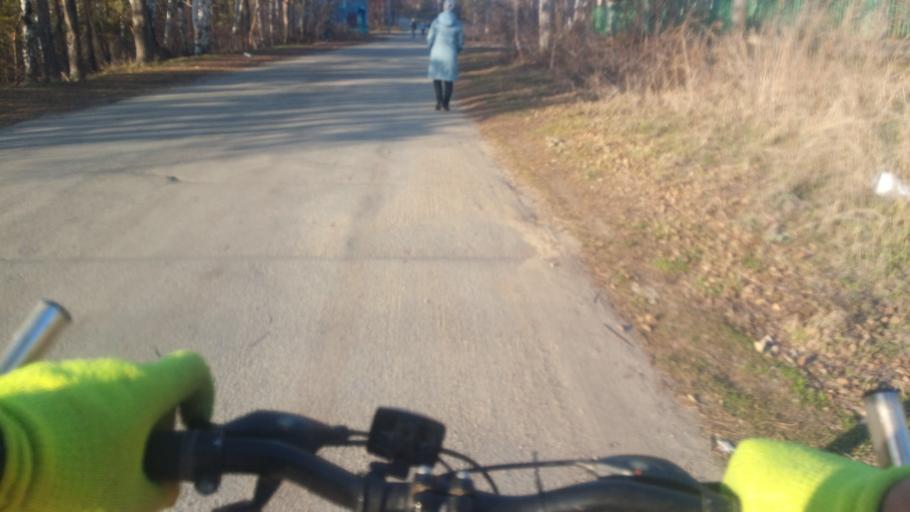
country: RU
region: Chelyabinsk
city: Novosineglazovskiy
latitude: 55.1250
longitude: 61.3296
